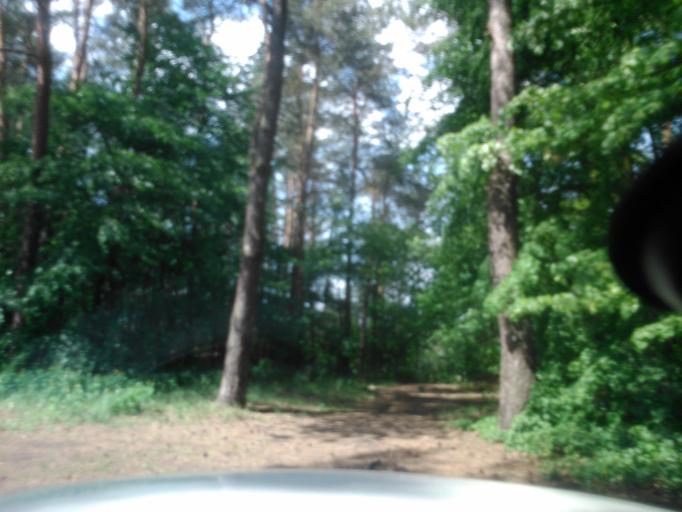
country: PL
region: Kujawsko-Pomorskie
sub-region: Powiat golubsko-dobrzynski
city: Golub-Dobrzyn
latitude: 53.1044
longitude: 19.0439
